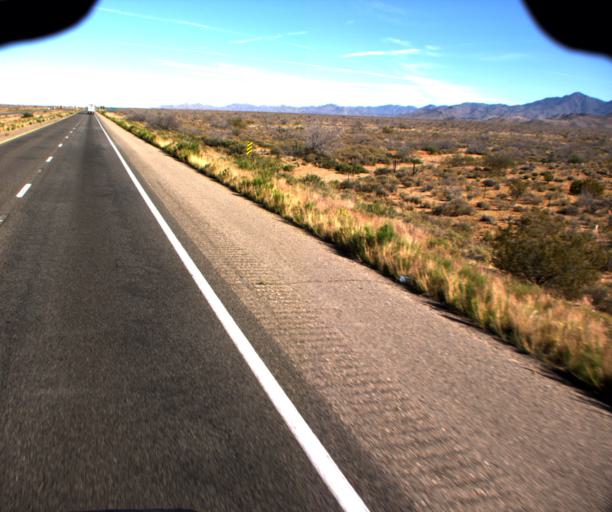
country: US
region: Arizona
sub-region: Mohave County
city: Golden Valley
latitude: 35.2755
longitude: -114.1712
